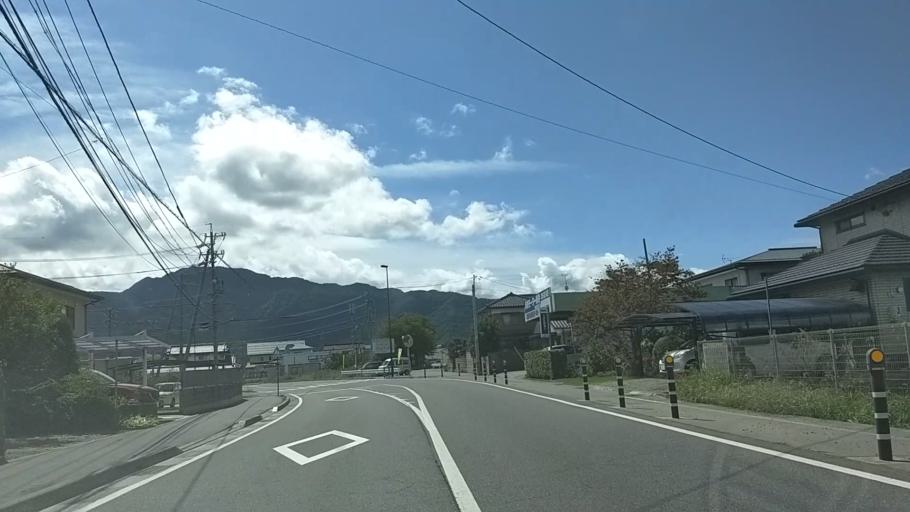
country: JP
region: Nagano
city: Suzaka
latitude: 36.6147
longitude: 138.2505
